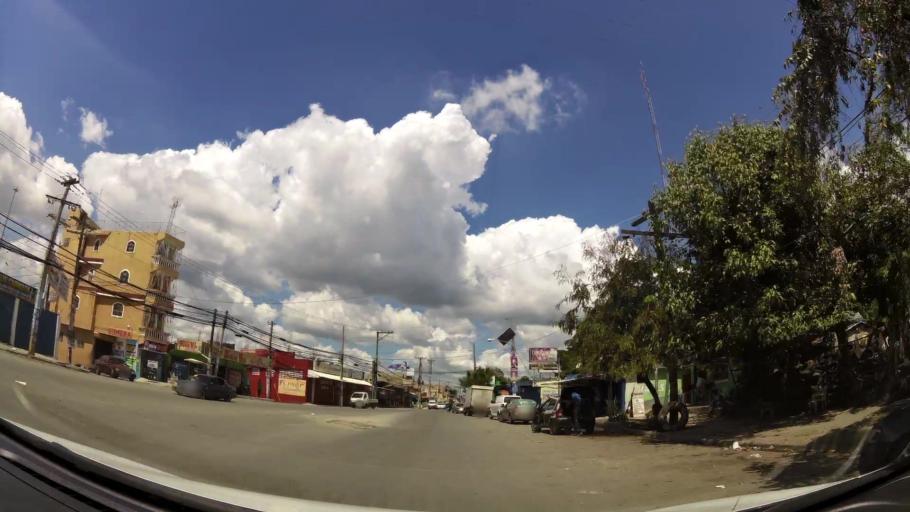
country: DO
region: Santo Domingo
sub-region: Santo Domingo
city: Santo Domingo Este
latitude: 18.5334
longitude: -69.8658
